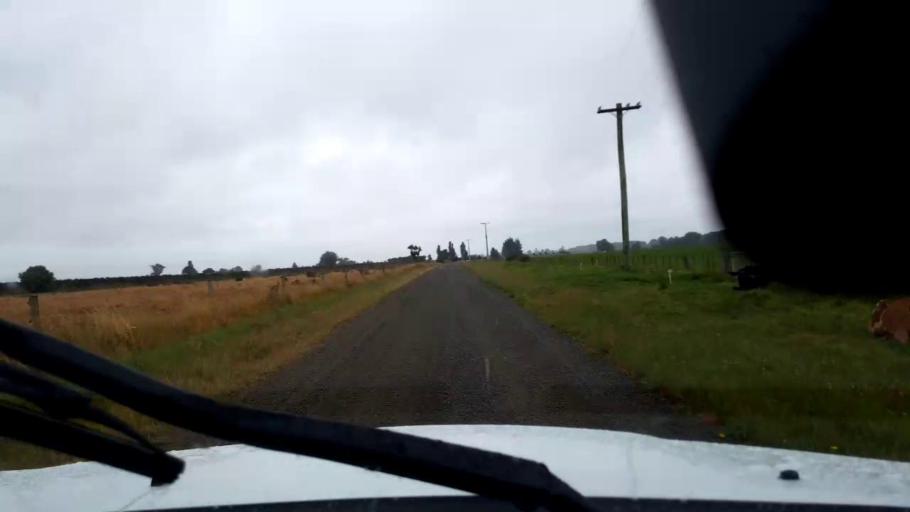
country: NZ
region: Canterbury
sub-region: Timaru District
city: Pleasant Point
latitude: -44.2534
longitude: 171.2090
